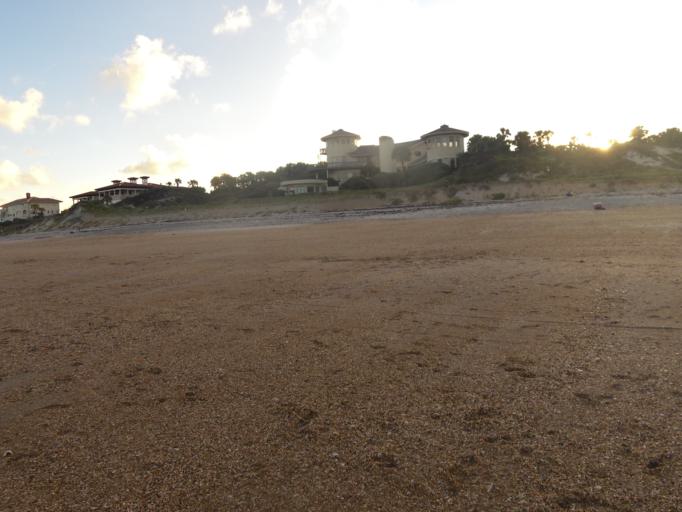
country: US
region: Florida
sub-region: Saint Johns County
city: Sawgrass
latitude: 30.1648
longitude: -81.3562
